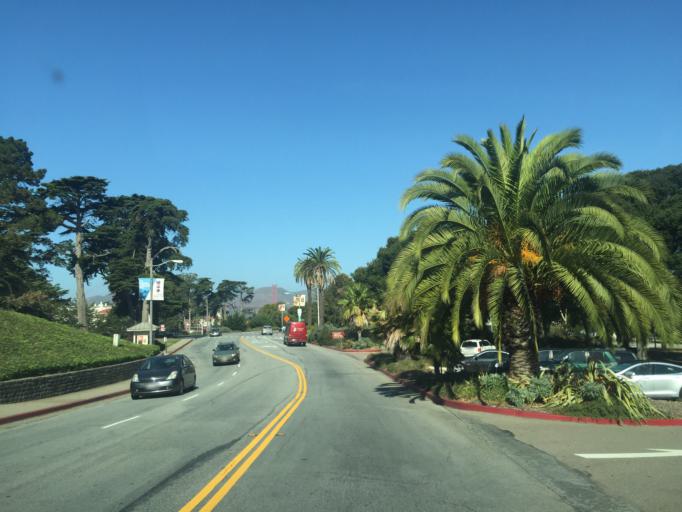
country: US
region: California
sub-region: San Francisco County
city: San Francisco
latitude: 37.7984
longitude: -122.4517
